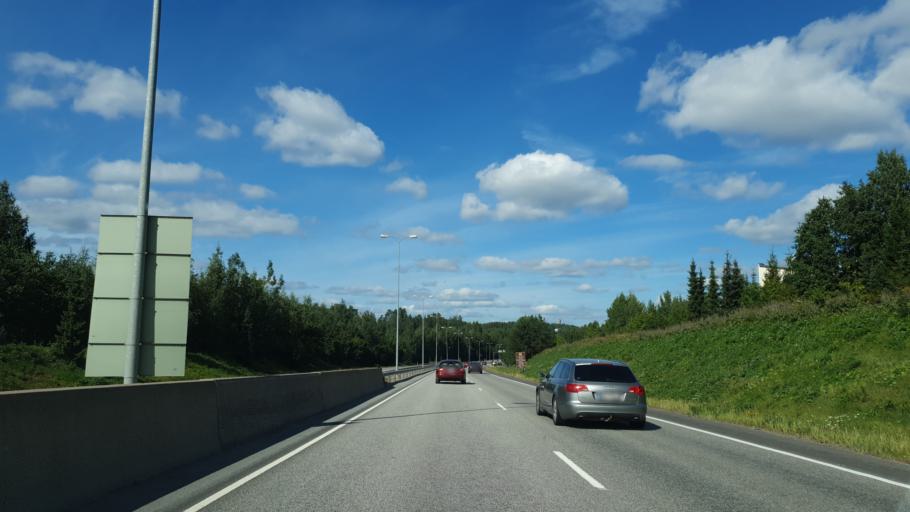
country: FI
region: Central Finland
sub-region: Jyvaeskylae
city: Jyvaeskylae
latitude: 62.2232
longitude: 25.7258
